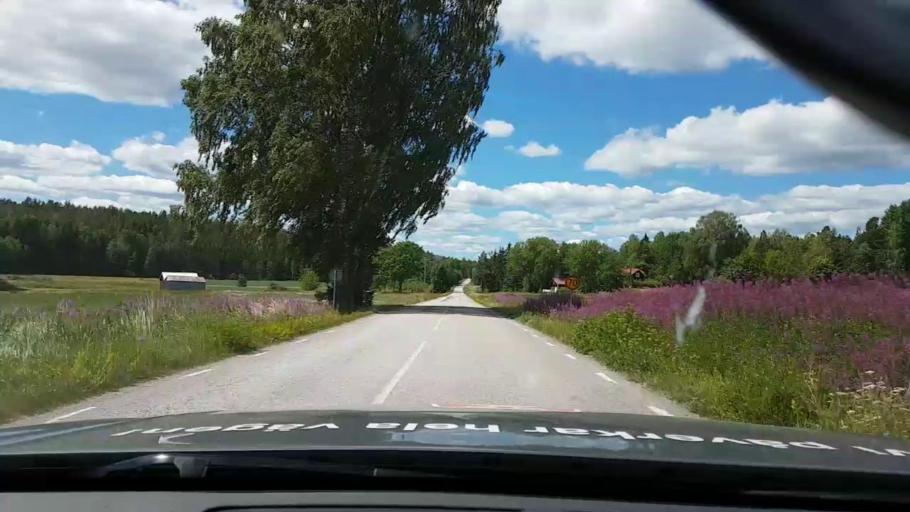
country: SE
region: Kalmar
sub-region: Vasterviks Kommun
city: Forserum
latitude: 58.0256
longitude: 16.5692
